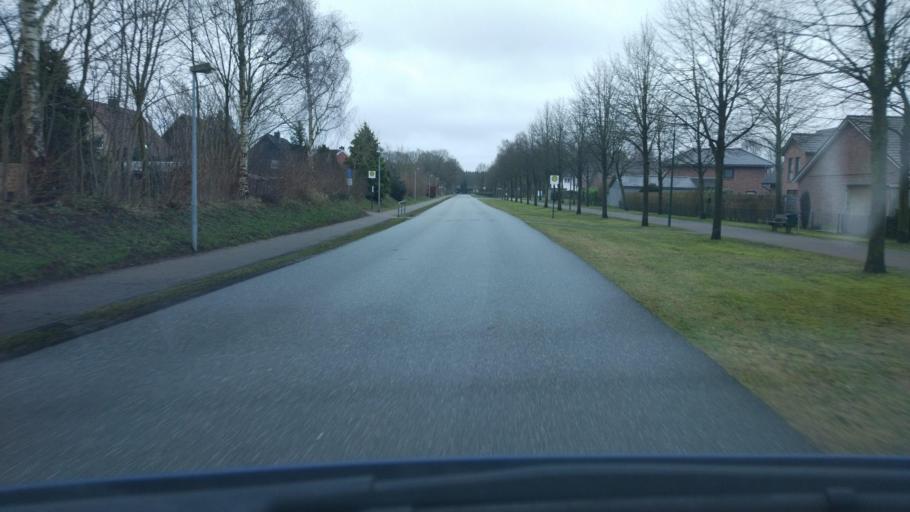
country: DE
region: Schleswig-Holstein
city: Kropp
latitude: 54.4126
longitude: 9.4959
